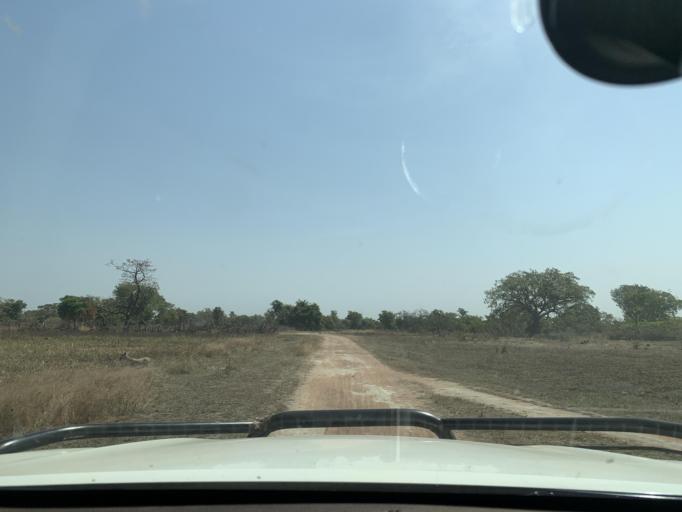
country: ML
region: Sikasso
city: Kolondieba
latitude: 10.8406
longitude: -6.8018
